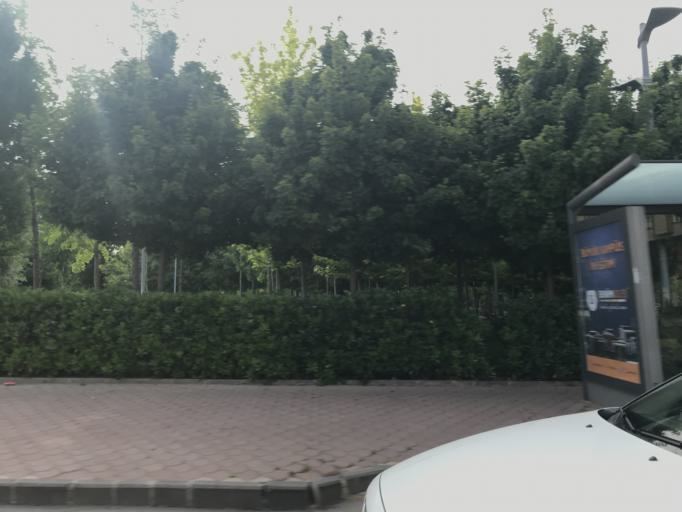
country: TR
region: Gaziantep
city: Sehitkamil
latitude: 37.0742
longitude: 37.3414
